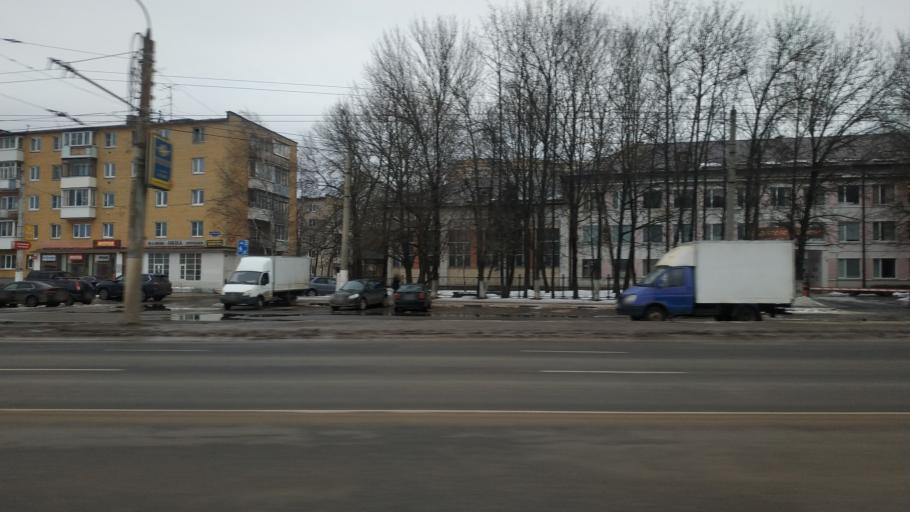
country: RU
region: Tverskaya
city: Tver
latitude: 56.8470
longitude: 35.9214
